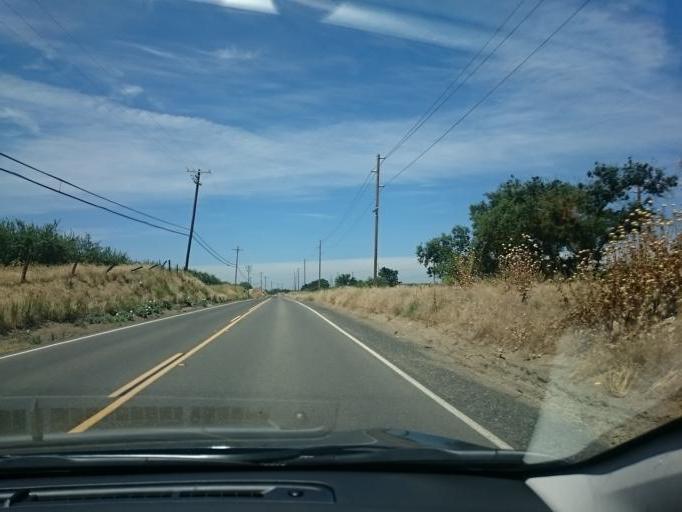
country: US
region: California
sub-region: Stanislaus County
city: Waterford
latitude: 37.6453
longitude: -120.6594
